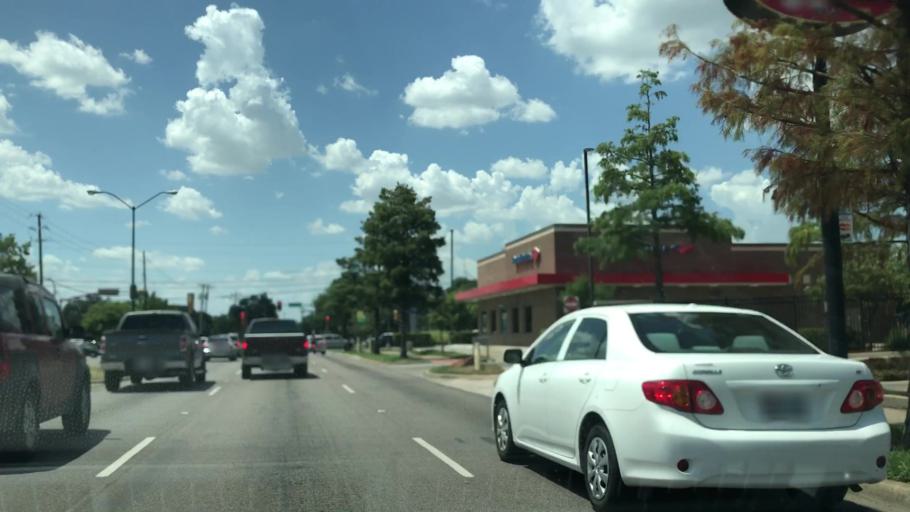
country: US
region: Texas
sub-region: Dallas County
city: University Park
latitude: 32.8293
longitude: -96.8256
